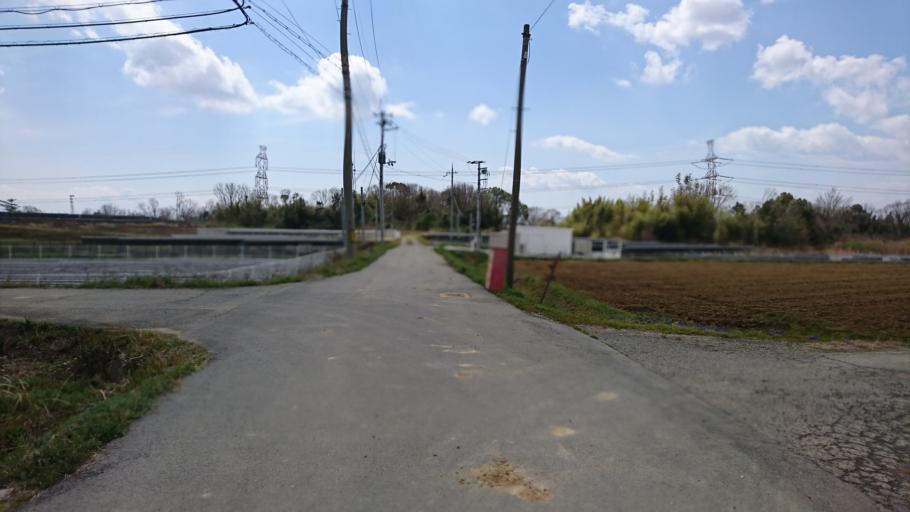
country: JP
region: Hyogo
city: Miki
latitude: 34.7702
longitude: 134.9573
